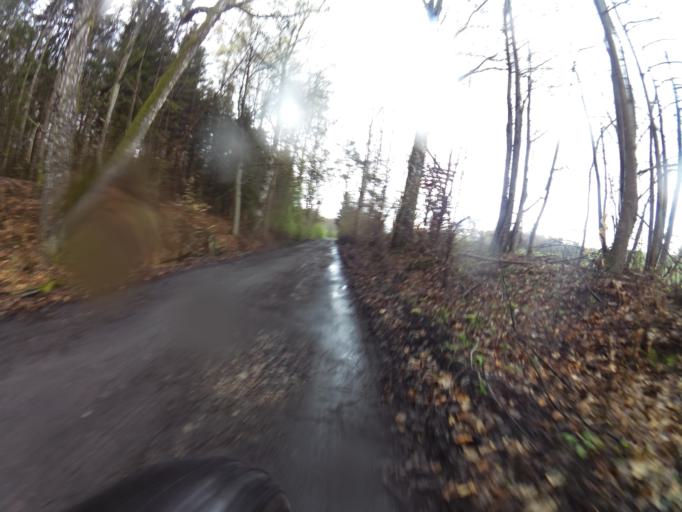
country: PL
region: Pomeranian Voivodeship
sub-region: Powiat slupski
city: Kepice
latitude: 54.2730
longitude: 16.7968
